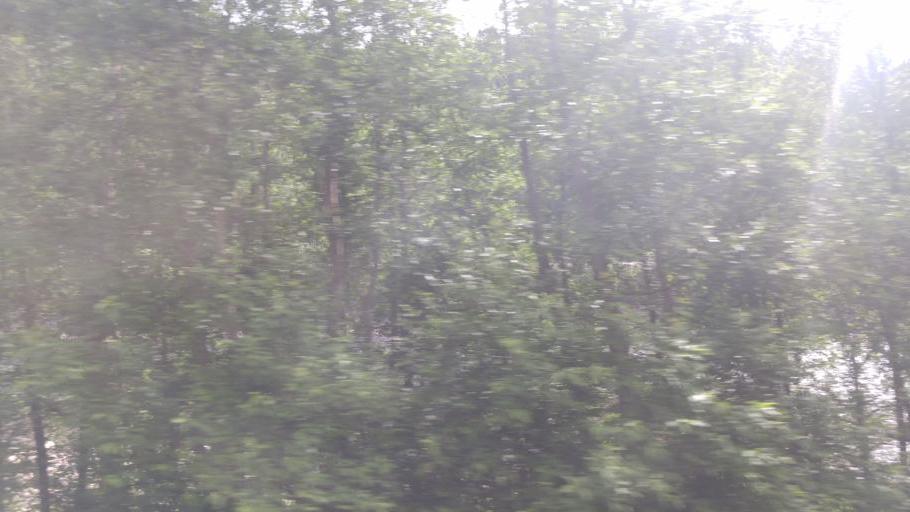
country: NO
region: Sor-Trondelag
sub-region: Midtre Gauldal
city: Storen
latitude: 63.0633
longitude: 10.2878
